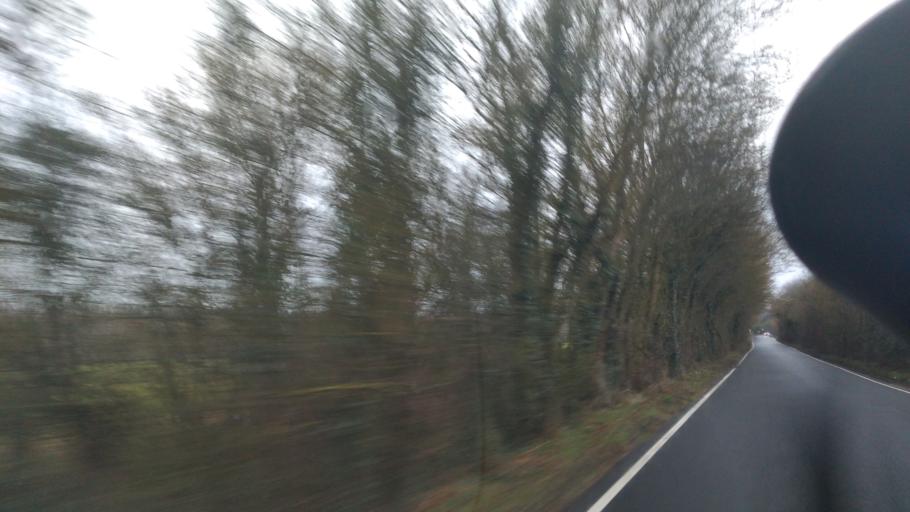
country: GB
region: England
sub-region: Oxfordshire
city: Shrivenham
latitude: 51.6166
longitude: -1.6784
